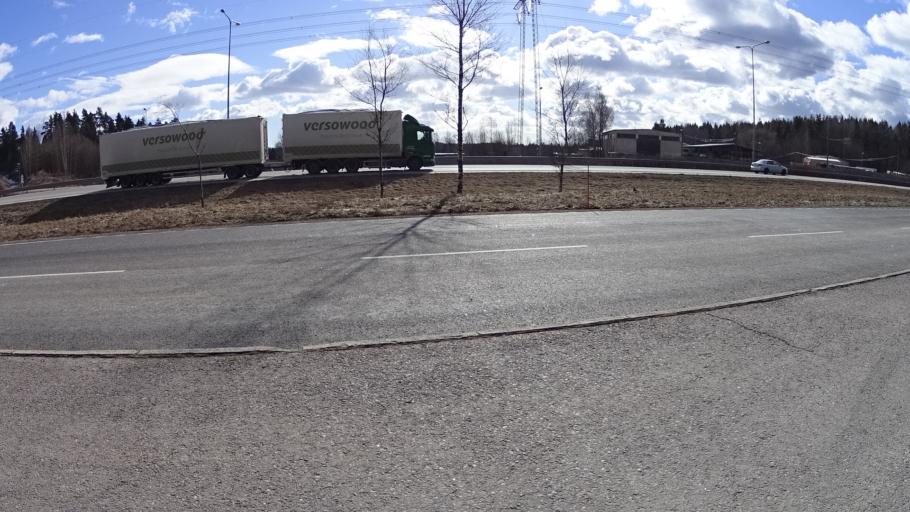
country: FI
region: Uusimaa
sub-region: Helsinki
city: Kauniainen
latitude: 60.2619
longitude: 24.7300
